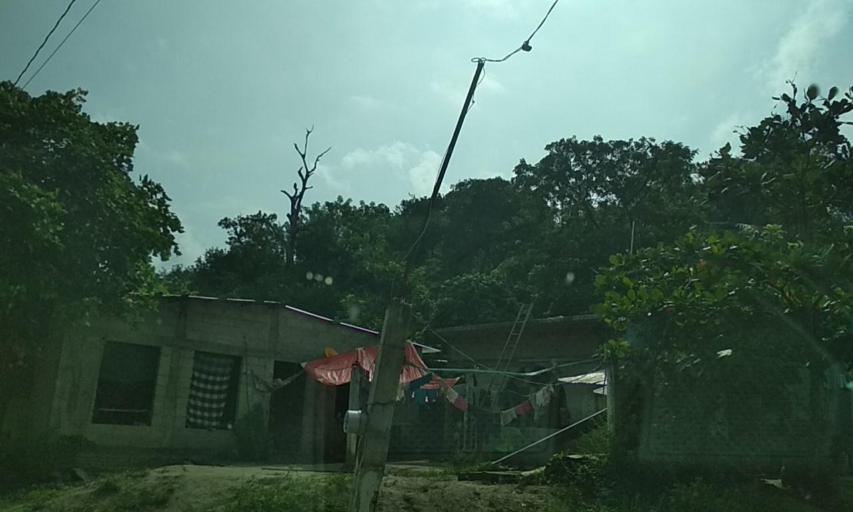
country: MX
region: Puebla
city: San Jose Acateno
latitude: 20.1606
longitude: -97.1827
